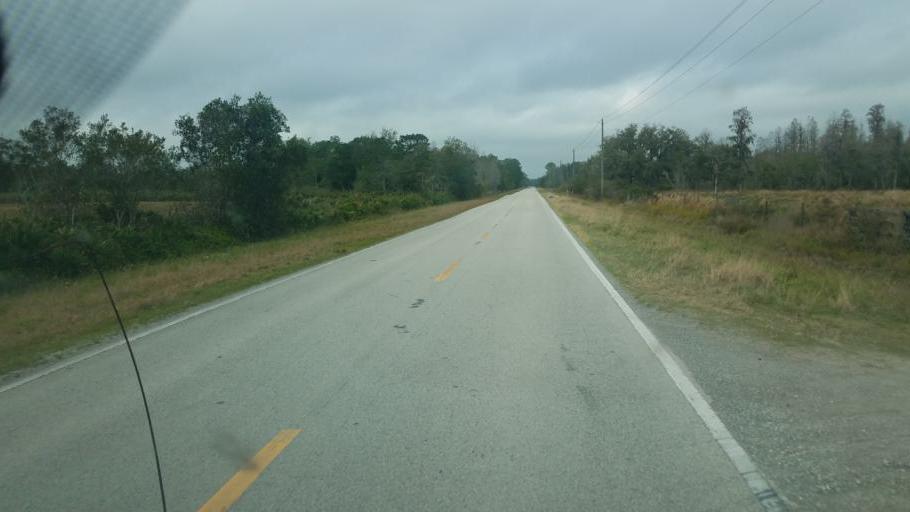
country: US
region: Florida
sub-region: Polk County
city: Polk City
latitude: 28.2590
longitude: -81.9361
